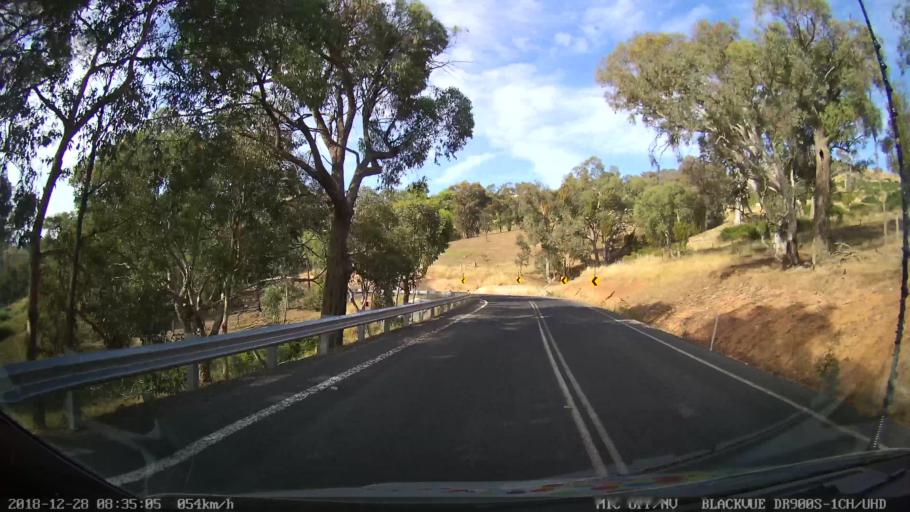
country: AU
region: New South Wales
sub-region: Blayney
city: Blayney
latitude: -33.9810
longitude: 149.3099
